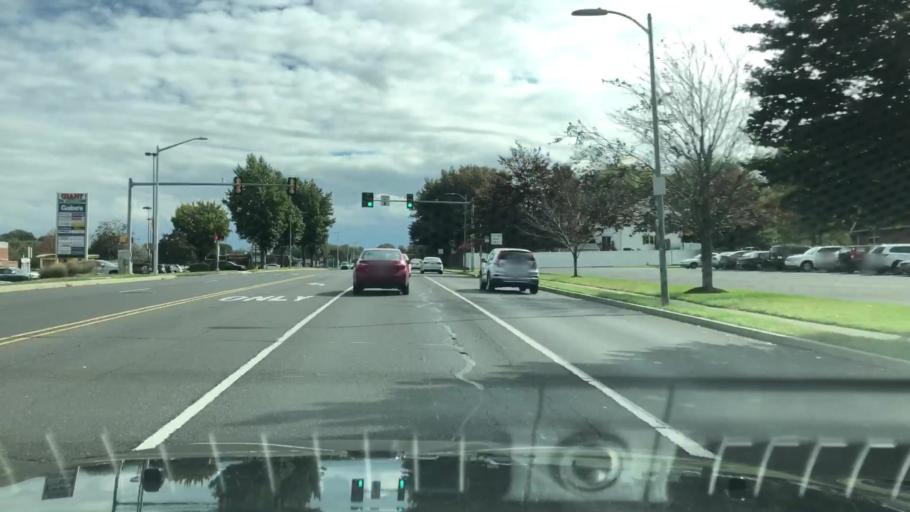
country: US
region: Pennsylvania
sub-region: Bucks County
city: Fairless Hills
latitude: 40.1721
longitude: -74.8531
